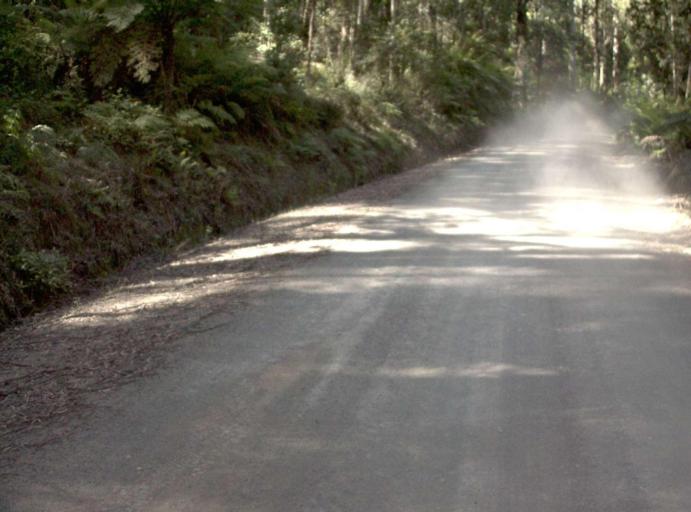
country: AU
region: New South Wales
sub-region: Bombala
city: Bombala
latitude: -37.2502
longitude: 148.7526
